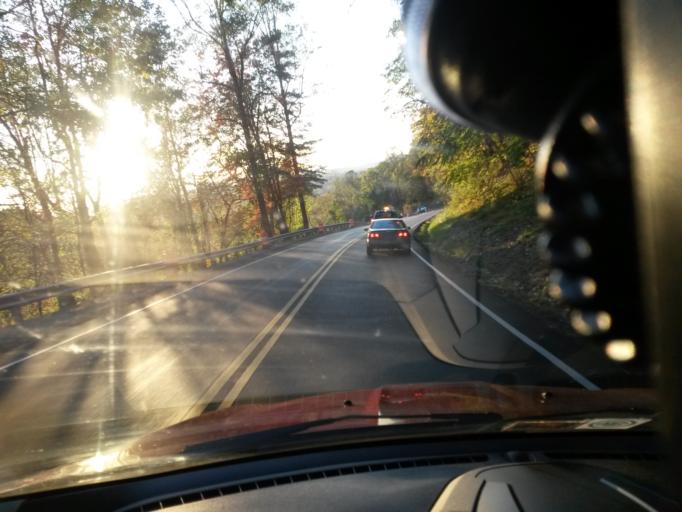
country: US
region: Virginia
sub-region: Roanoke County
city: Narrows
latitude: 37.1840
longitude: -79.8798
